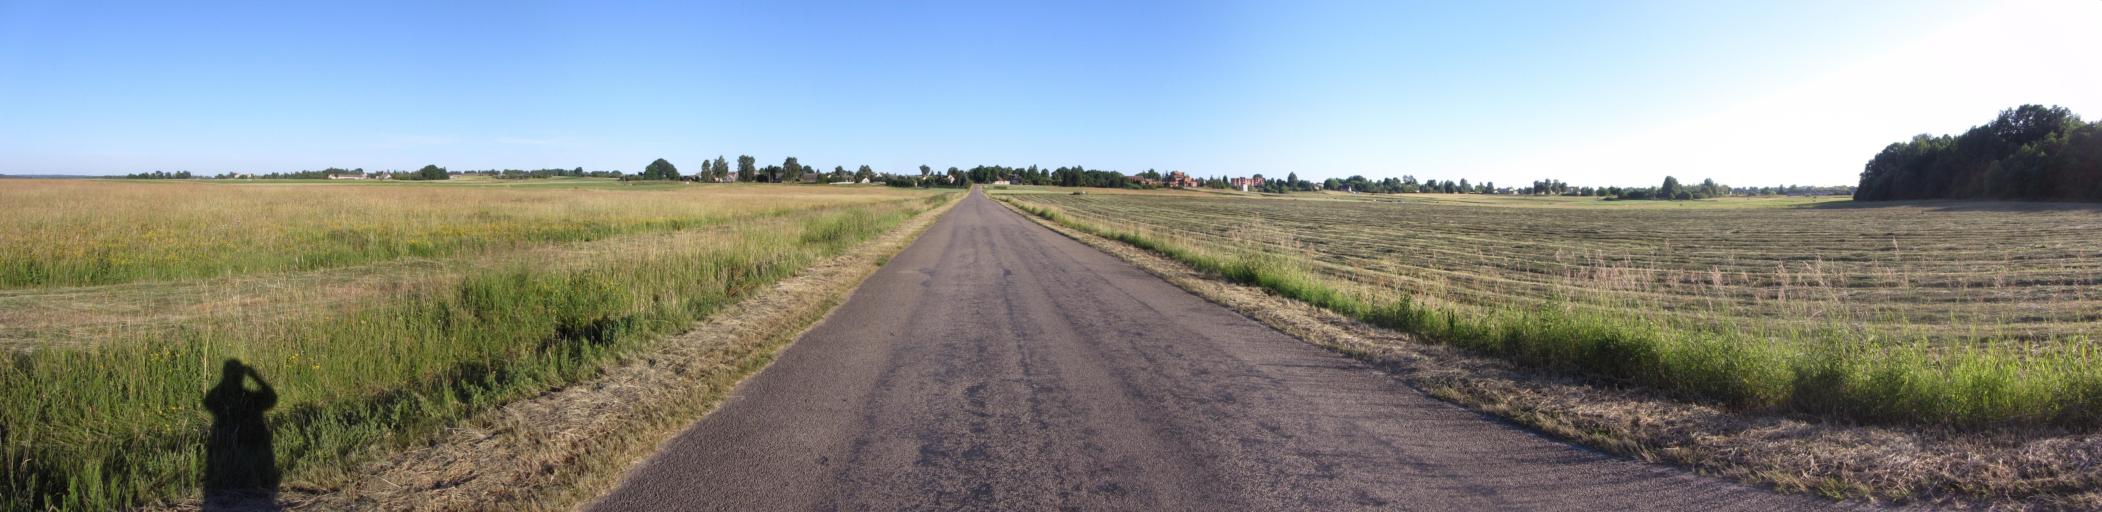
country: LT
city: Jieznas
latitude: 54.5458
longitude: 24.3318
